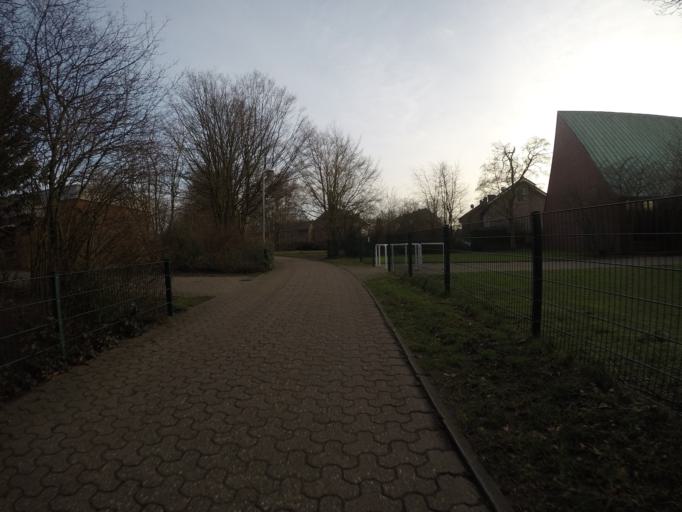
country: DE
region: North Rhine-Westphalia
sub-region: Regierungsbezirk Dusseldorf
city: Bocholt
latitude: 51.8250
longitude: 6.6179
